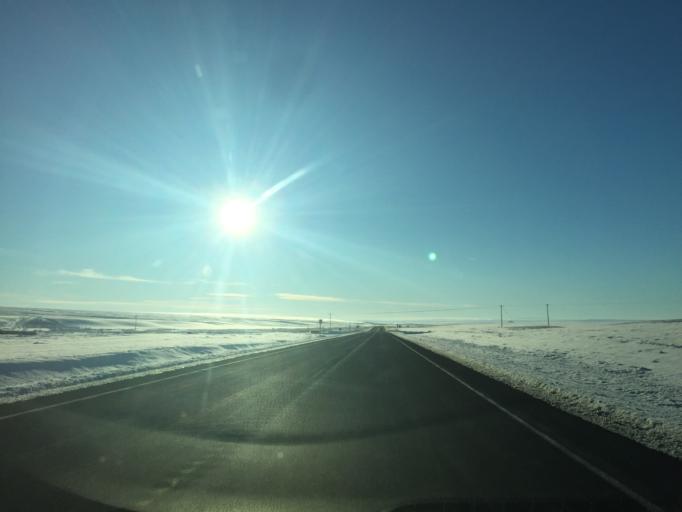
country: US
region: Washington
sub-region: Okanogan County
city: Coulee Dam
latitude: 47.6913
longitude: -118.9730
